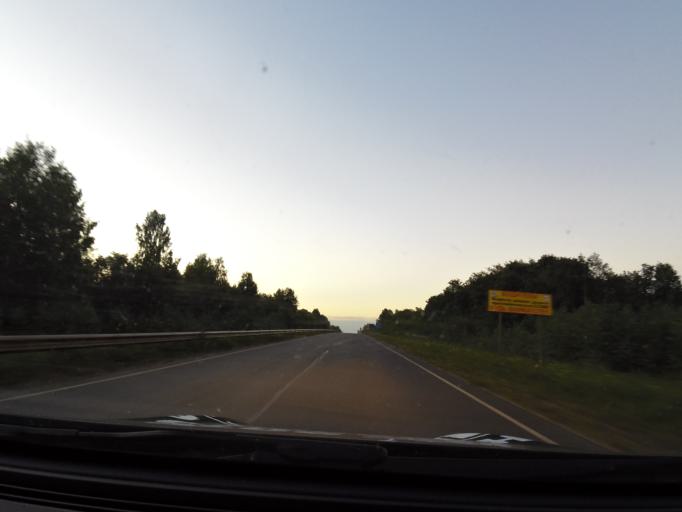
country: RU
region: Vologda
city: Vytegra
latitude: 60.9893
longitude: 36.1112
